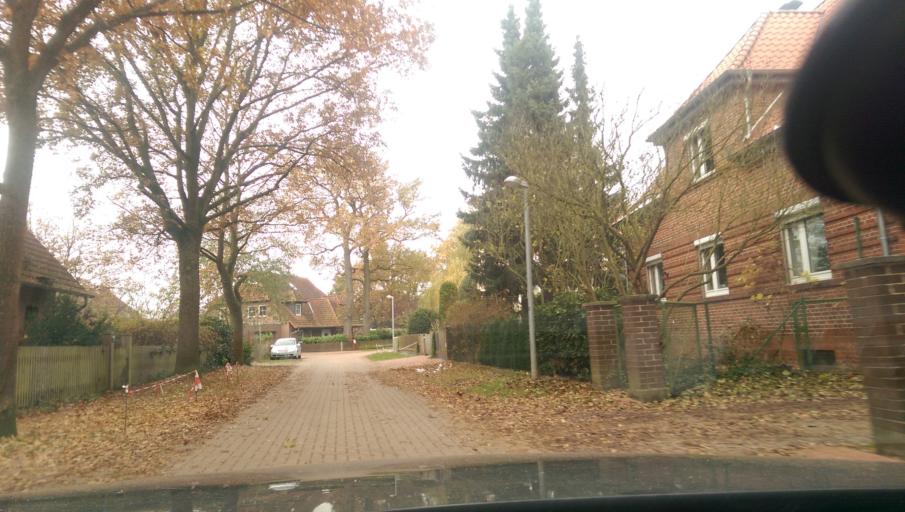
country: DE
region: Lower Saxony
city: Lindwedel
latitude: 52.5563
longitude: 9.6805
